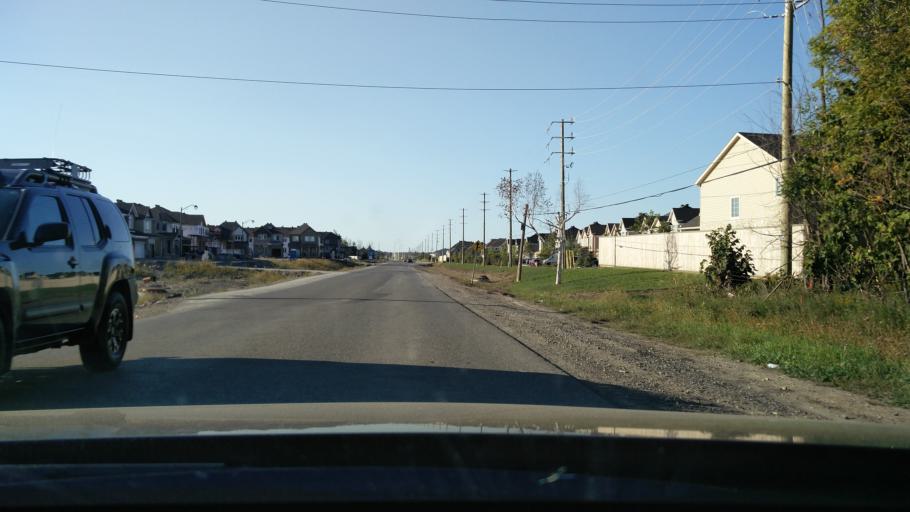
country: CA
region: Ontario
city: Bells Corners
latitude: 45.2389
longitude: -75.7276
